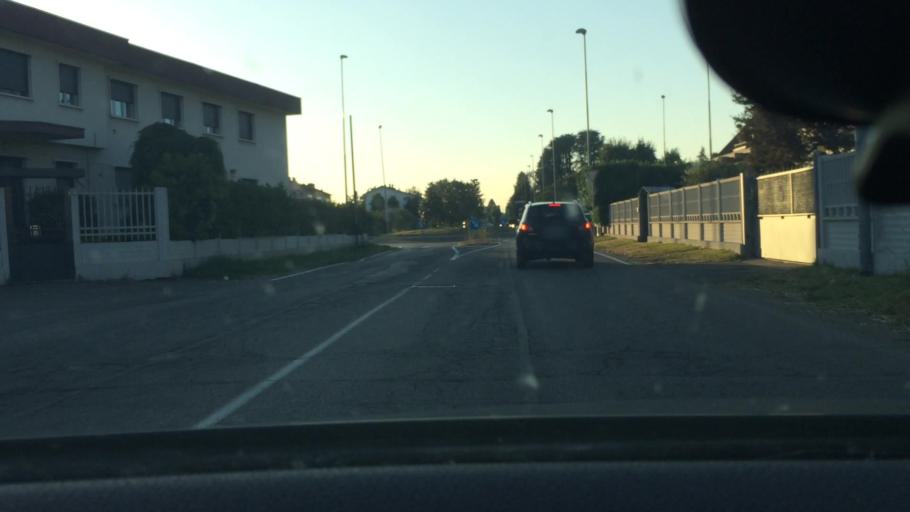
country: IT
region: Lombardy
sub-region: Citta metropolitana di Milano
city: Rescaldina
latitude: 45.6140
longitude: 8.9611
